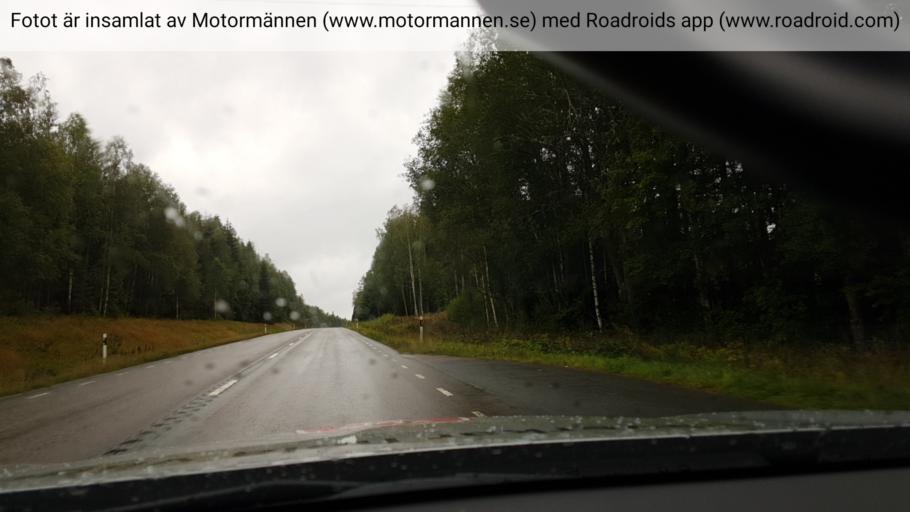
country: SE
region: Vaestra Goetaland
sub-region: Bengtsfors Kommun
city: Billingsfors
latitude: 58.9351
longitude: 12.1846
